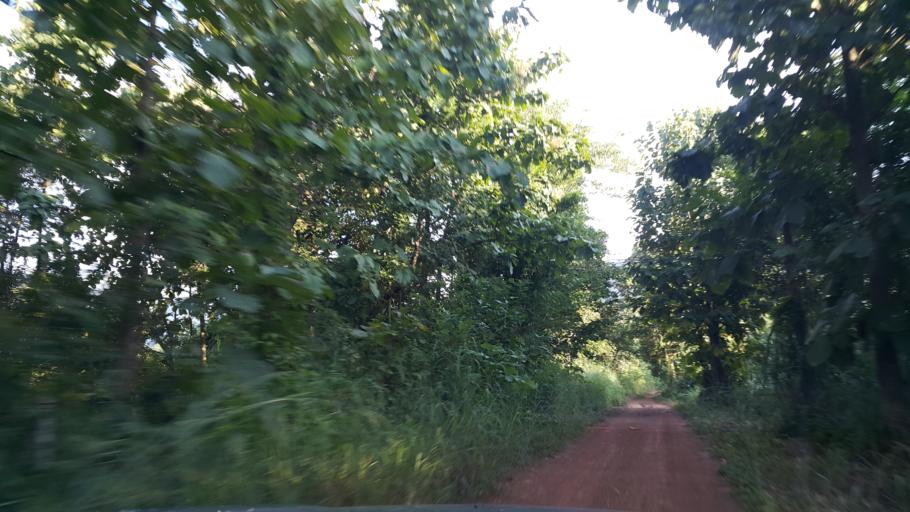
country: TH
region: Chiang Mai
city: Mae On
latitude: 18.7438
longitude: 99.2474
